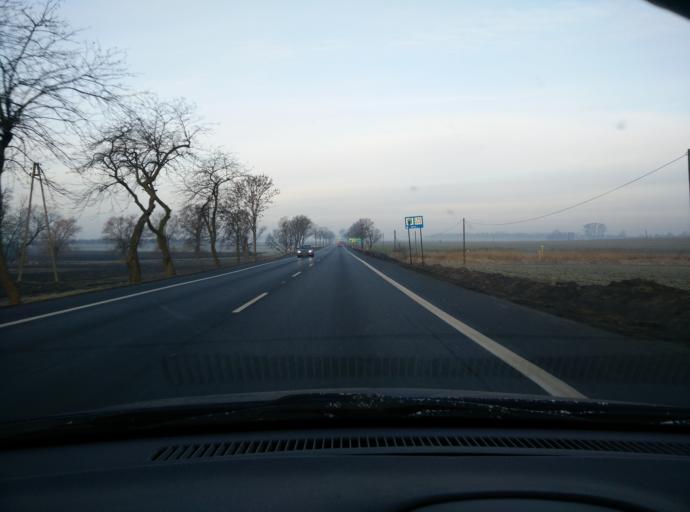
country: PL
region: Greater Poland Voivodeship
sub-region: Powiat poznanski
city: Kornik
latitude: 52.2420
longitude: 17.1401
